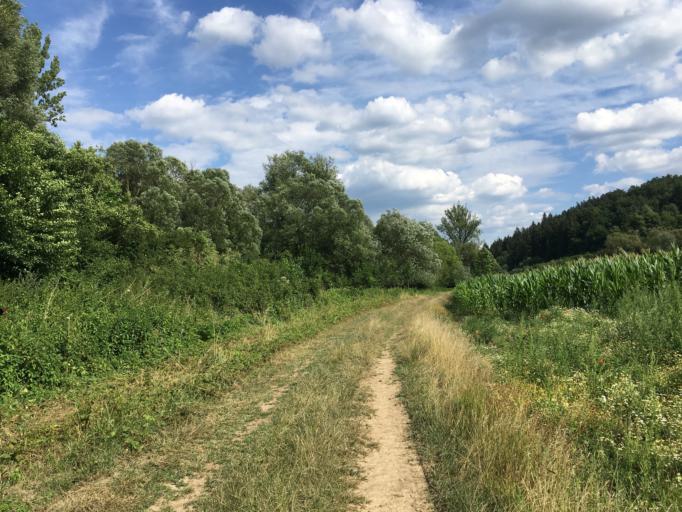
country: SK
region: Trenciansky
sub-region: Okres Povazska Bystrica
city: Povazska Bystrica
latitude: 49.0637
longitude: 18.3843
